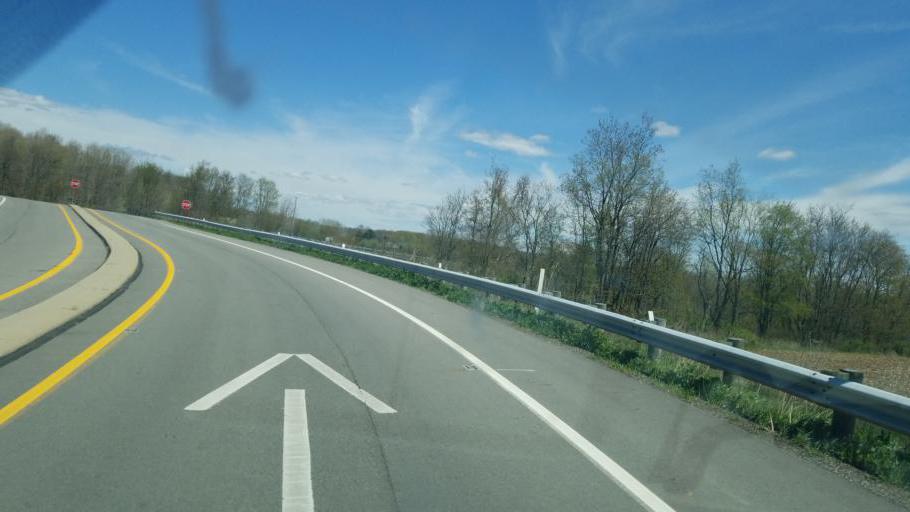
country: US
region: Ohio
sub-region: Richland County
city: Lincoln Heights
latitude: 40.7358
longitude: -82.4583
